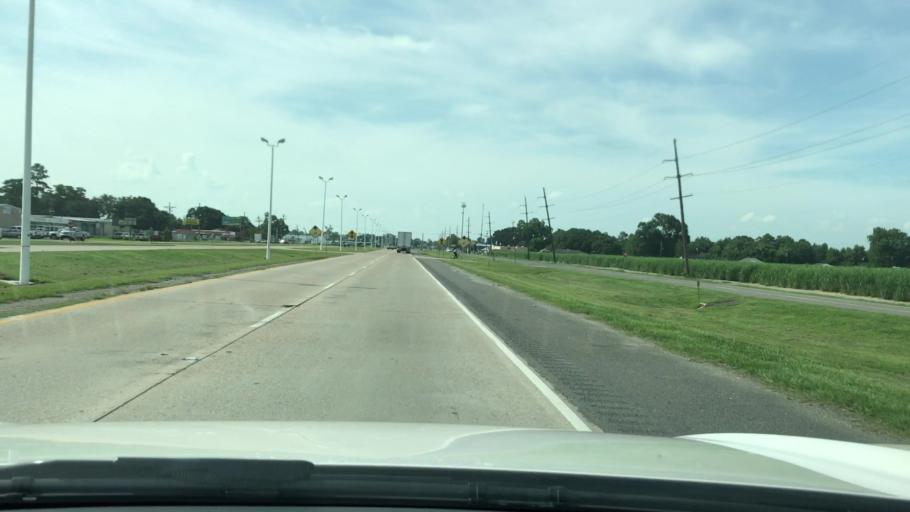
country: US
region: Louisiana
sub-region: West Baton Rouge Parish
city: Addis
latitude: 30.3522
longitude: -91.2583
